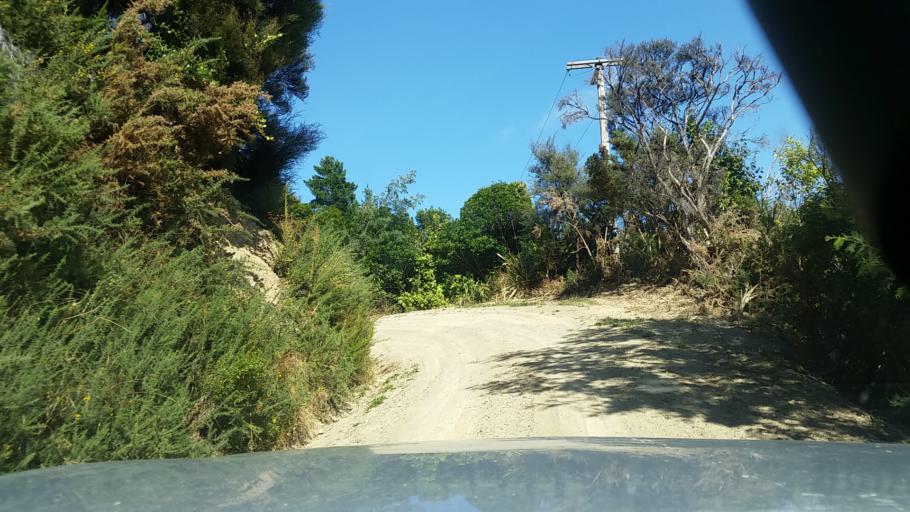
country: NZ
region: Marlborough
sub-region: Marlborough District
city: Picton
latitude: -41.3073
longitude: 174.1736
